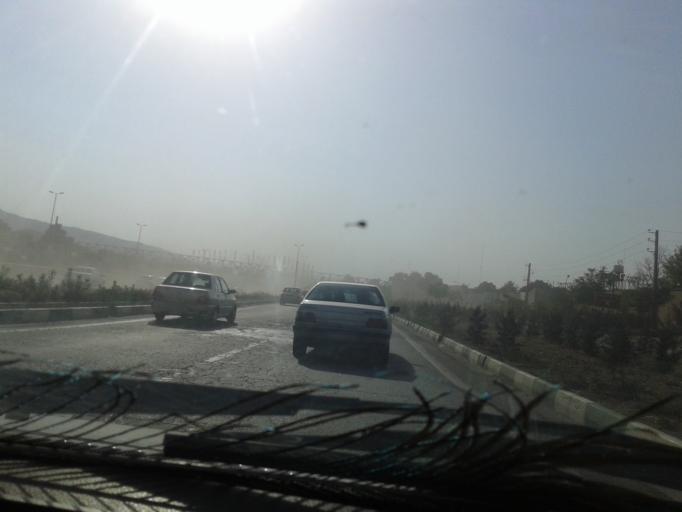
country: IR
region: Tehran
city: Tehran
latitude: 35.7244
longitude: 51.6036
